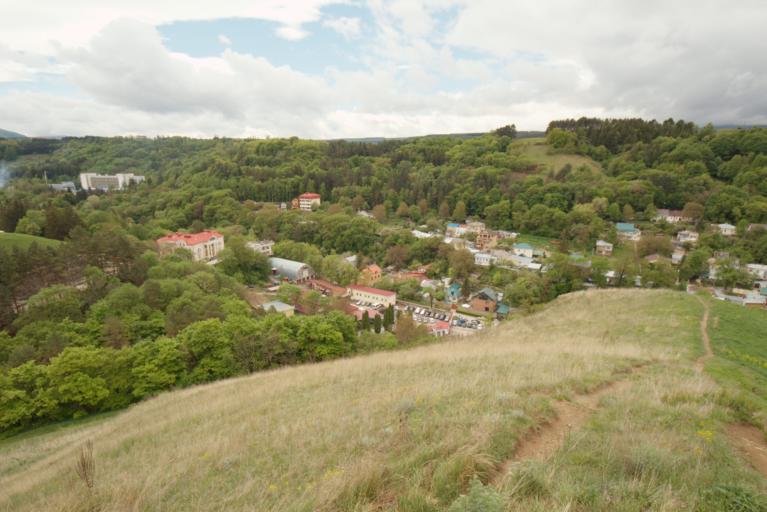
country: RU
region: Stavropol'skiy
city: Kislovodsk
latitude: 43.8924
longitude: 42.7236
